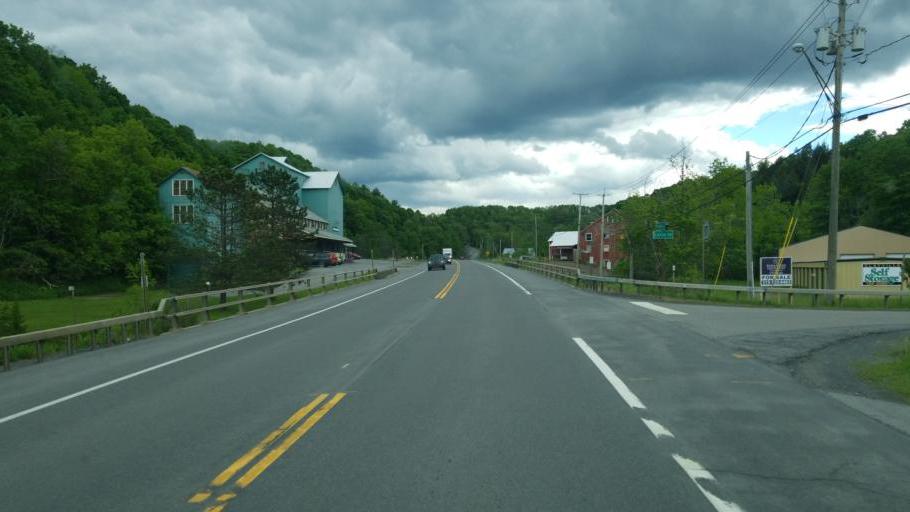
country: US
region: New York
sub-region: Oneida County
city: Chadwicks
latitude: 42.9593
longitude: -75.2443
